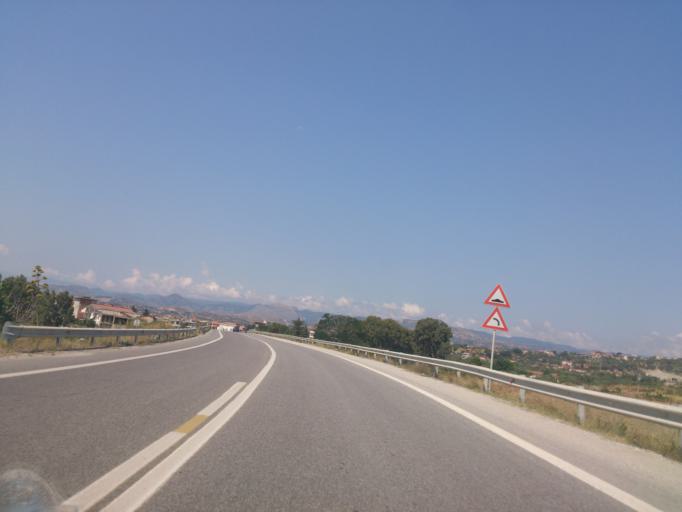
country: IT
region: Calabria
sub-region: Provincia di Reggio Calabria
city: Marina di Gioiosa Ionica
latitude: 38.3067
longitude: 16.3449
